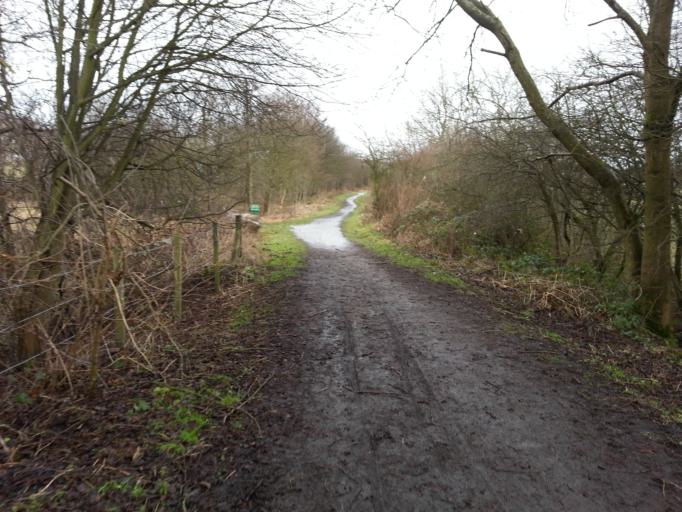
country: GB
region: England
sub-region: County Durham
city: Crook
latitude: 54.7578
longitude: -1.7305
